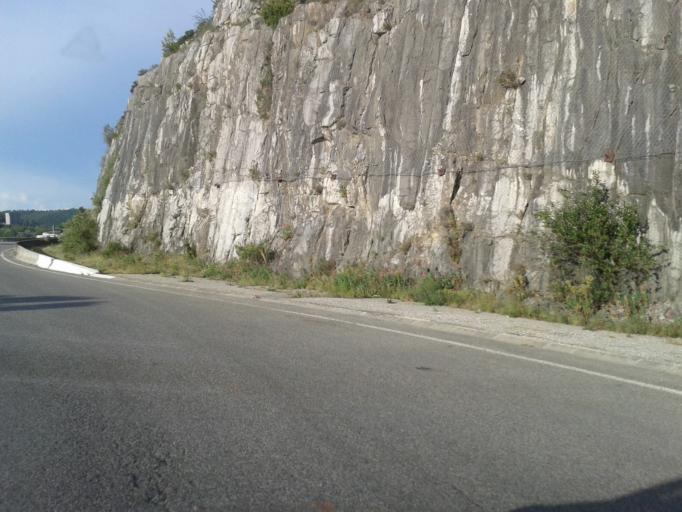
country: FR
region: Provence-Alpes-Cote d'Azur
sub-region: Departement du Vaucluse
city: Beaumont-de-Pertuis
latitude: 43.6886
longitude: 5.6671
